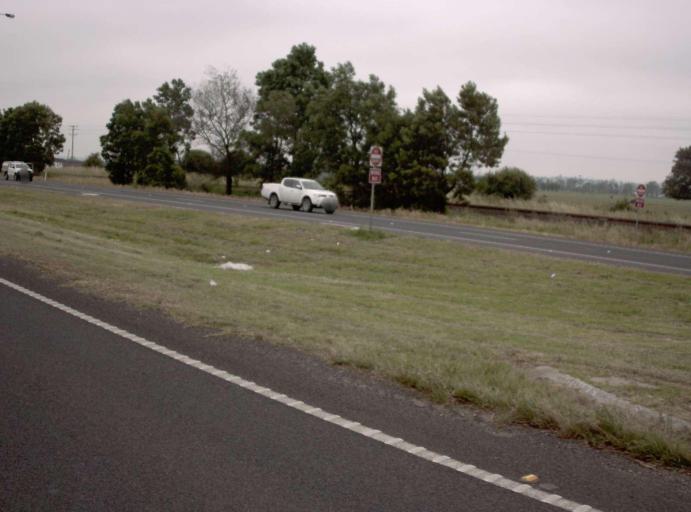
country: AU
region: Victoria
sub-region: Latrobe
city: Moe
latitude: -38.2096
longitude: 146.1355
